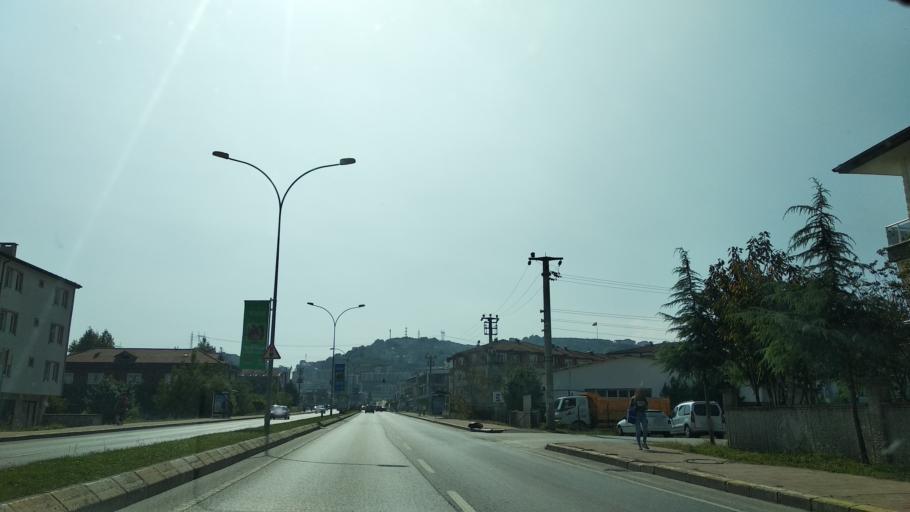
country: TR
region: Sakarya
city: Adapazari
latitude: 40.7639
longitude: 30.3633
